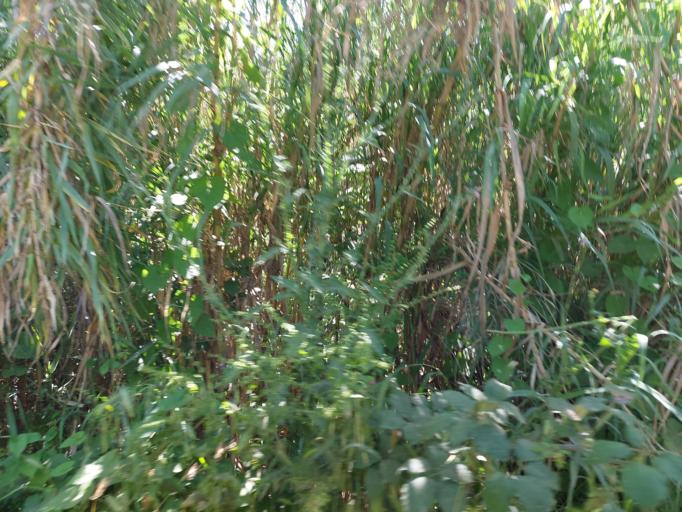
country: IT
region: Latium
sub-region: Citta metropolitana di Roma Capitale
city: Rome
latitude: 41.8539
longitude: 12.5509
